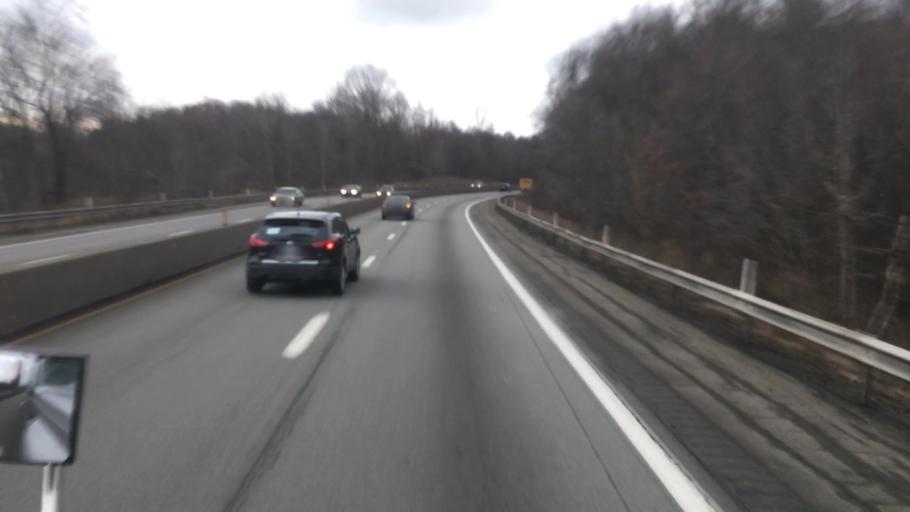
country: US
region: Pennsylvania
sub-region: Westmoreland County
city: New Stanton
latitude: 40.1941
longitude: -79.6865
